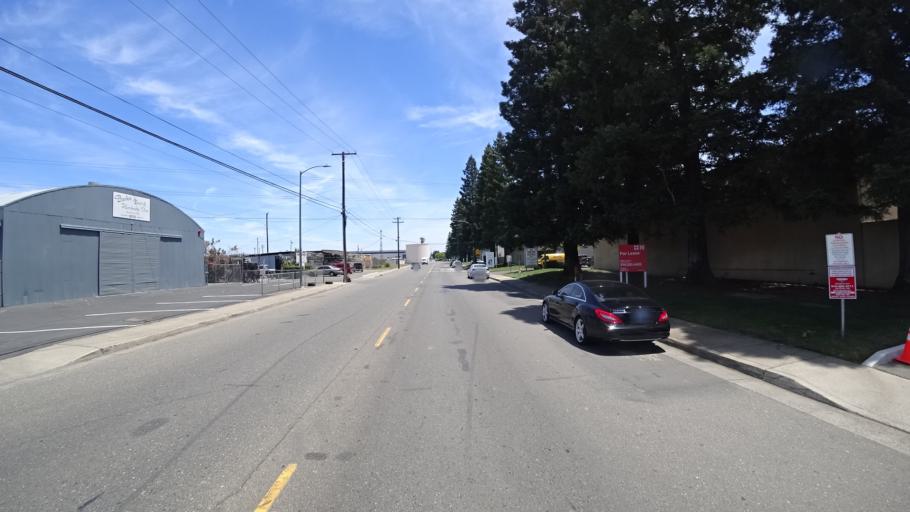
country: US
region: California
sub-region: Sacramento County
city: Rosemont
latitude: 38.5380
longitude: -121.4018
